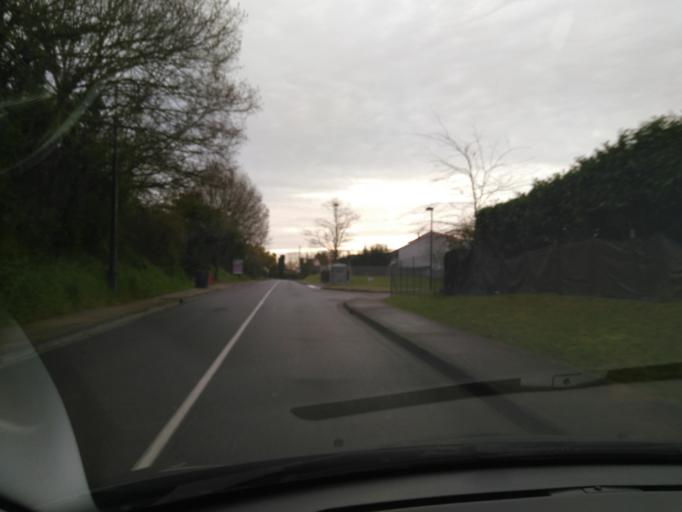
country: FR
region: Midi-Pyrenees
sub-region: Departement de la Haute-Garonne
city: Castelnau-d'Estretefonds
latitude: 43.7803
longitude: 1.3622
